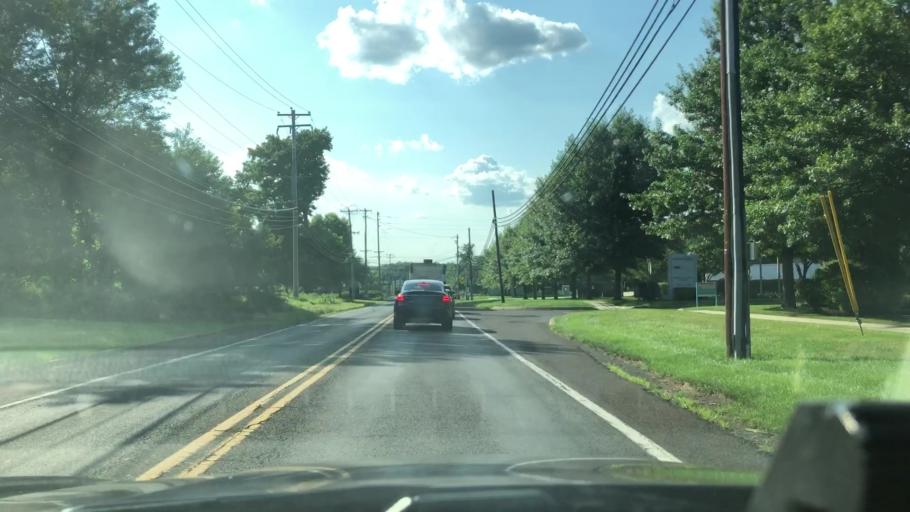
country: US
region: Pennsylvania
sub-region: Montgomery County
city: Montgomeryville
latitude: 40.2743
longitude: -75.2429
